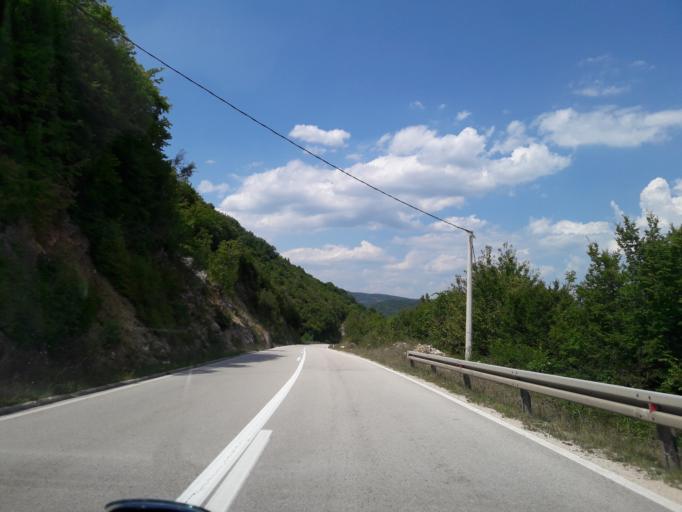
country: BA
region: Republika Srpska
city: Mrkonjic Grad
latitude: 44.5200
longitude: 17.1512
